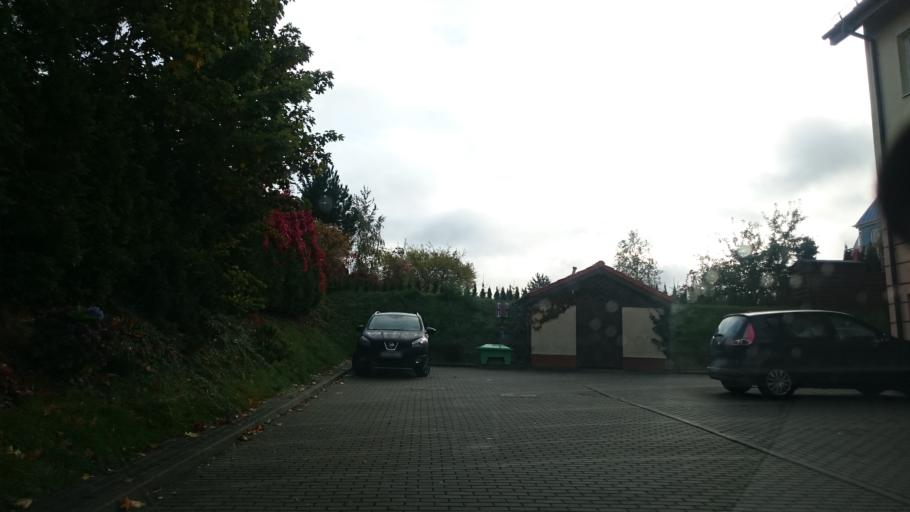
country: PL
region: Pomeranian Voivodeship
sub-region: Gdynia
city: Wielki Kack
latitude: 54.4636
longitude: 18.4954
